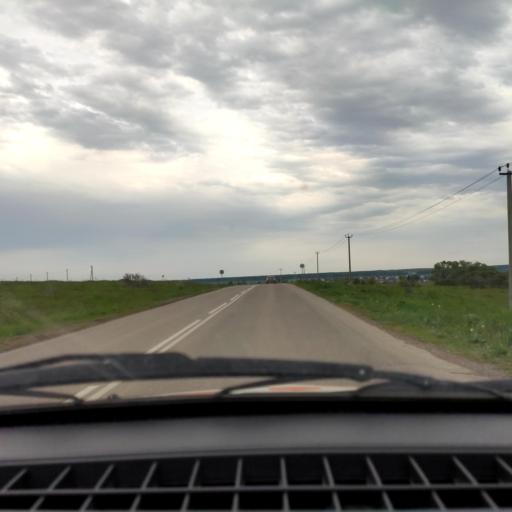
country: RU
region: Bashkortostan
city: Avdon
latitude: 54.5640
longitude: 55.7605
